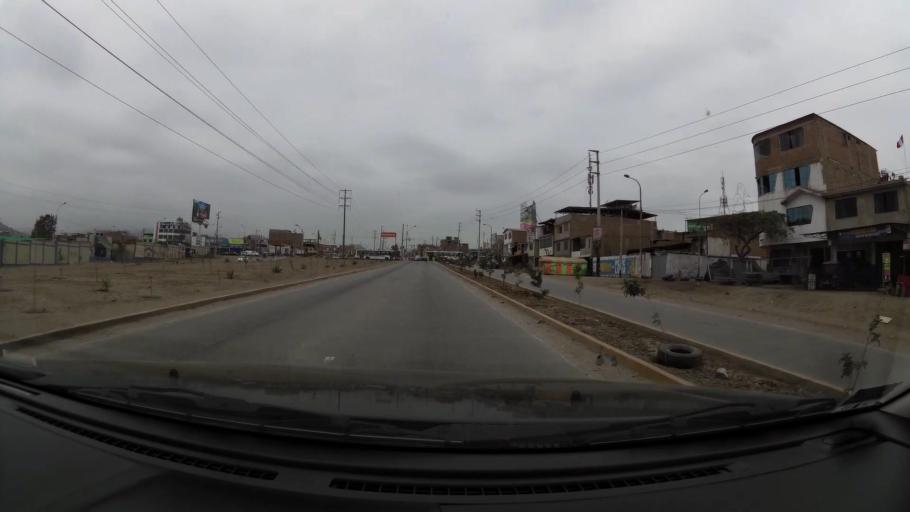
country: PE
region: Lima
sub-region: Lima
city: Surco
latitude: -12.2065
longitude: -76.9542
